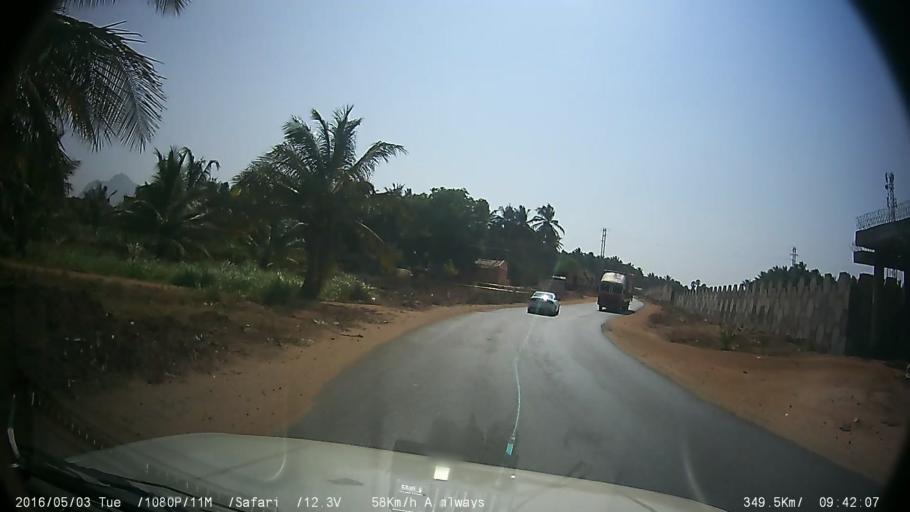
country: IN
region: Tamil Nadu
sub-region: Coimbatore
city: Madukkarai
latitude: 10.8551
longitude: 76.8477
